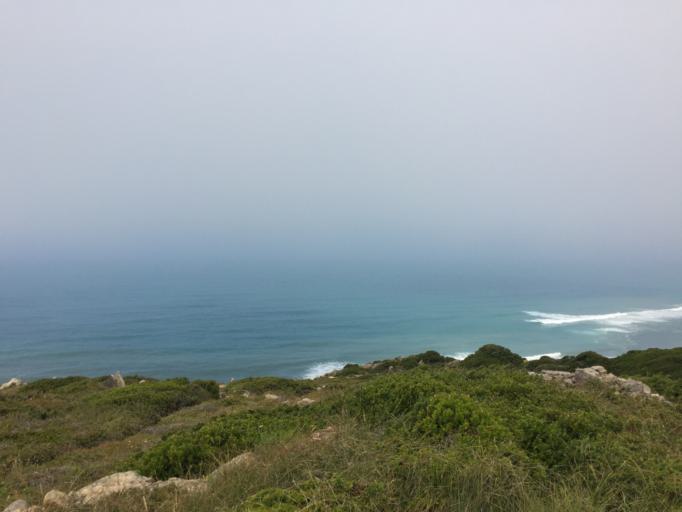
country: PT
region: Lisbon
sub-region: Sintra
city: Colares
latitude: 38.8092
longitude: -9.4796
